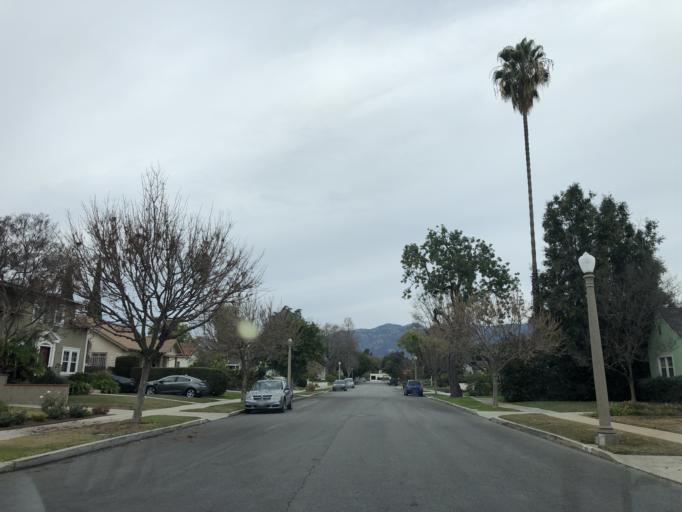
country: US
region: California
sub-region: Los Angeles County
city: San Gabriel
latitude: 34.1050
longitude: -118.1079
